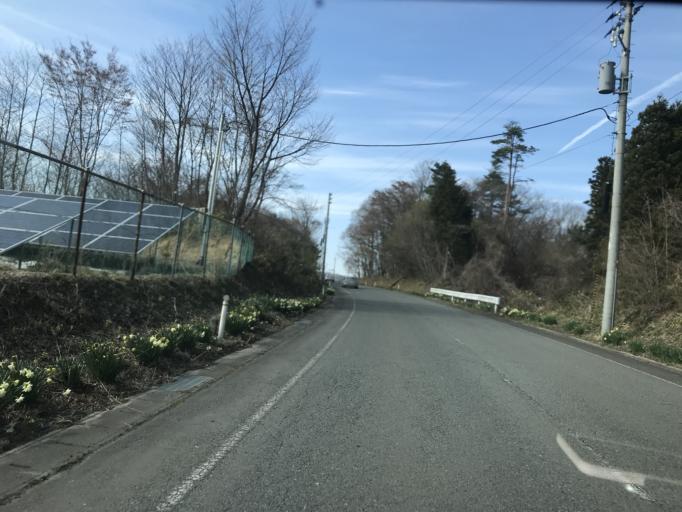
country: JP
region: Iwate
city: Ichinoseki
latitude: 38.8897
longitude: 141.3886
